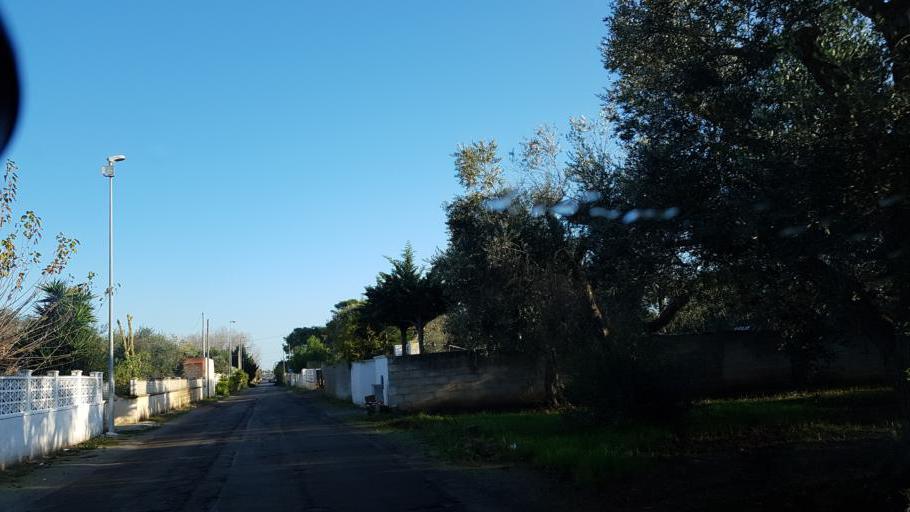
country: IT
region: Apulia
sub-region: Provincia di Brindisi
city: Torchiarolo
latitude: 40.5030
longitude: 18.1093
